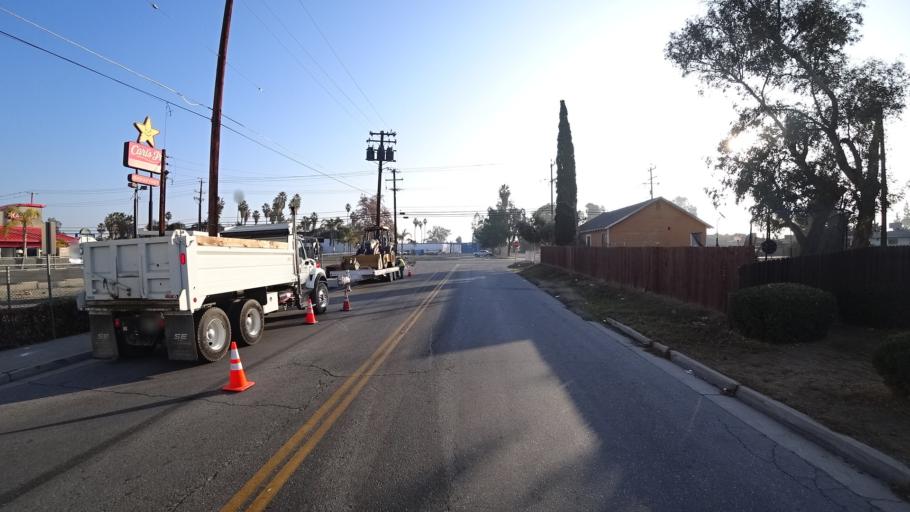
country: US
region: California
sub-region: Kern County
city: Bakersfield
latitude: 35.3652
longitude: -119.0440
